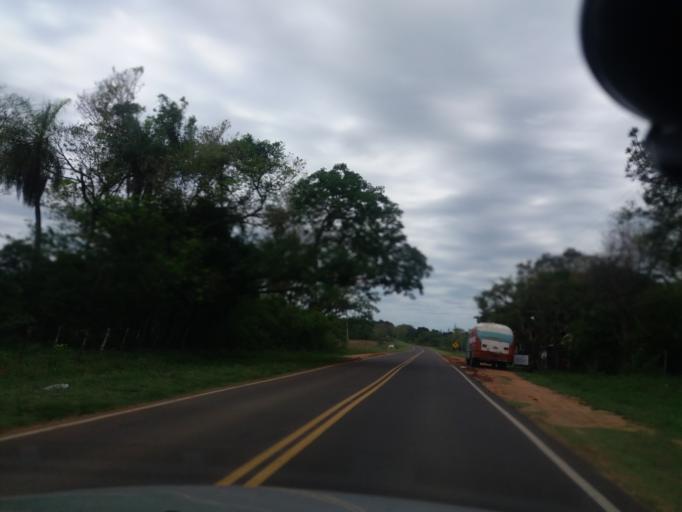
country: AR
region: Corrientes
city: Riachuelo
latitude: -27.4566
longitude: -58.7003
